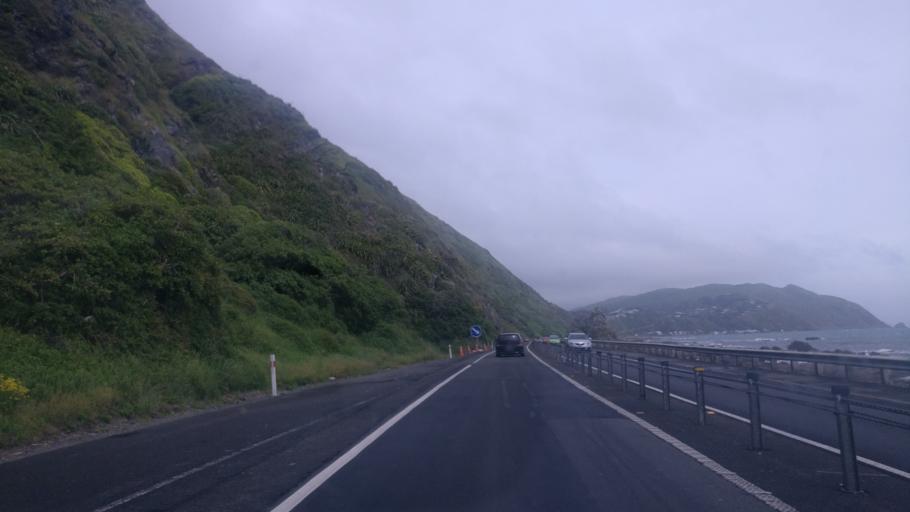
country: NZ
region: Wellington
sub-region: Porirua City
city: Porirua
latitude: -41.0197
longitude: 174.9121
